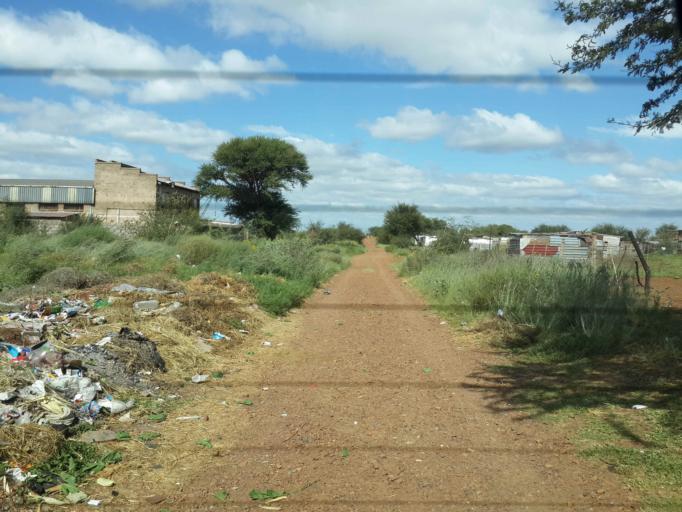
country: ZA
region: Northern Cape
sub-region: Siyanda District Municipality
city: Danielskuil
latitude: -28.1925
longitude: 23.5428
